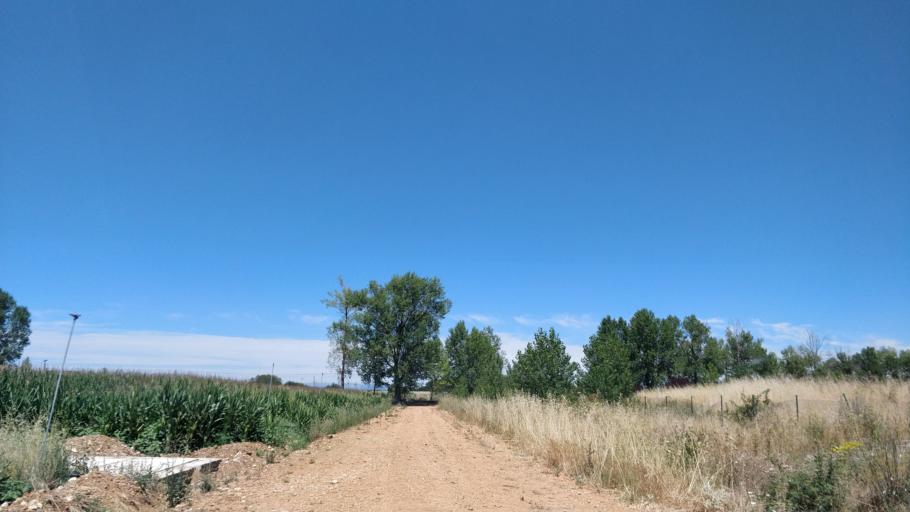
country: ES
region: Castille and Leon
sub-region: Provincia de Leon
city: Bustillo del Paramo
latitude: 42.4782
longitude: -5.8112
